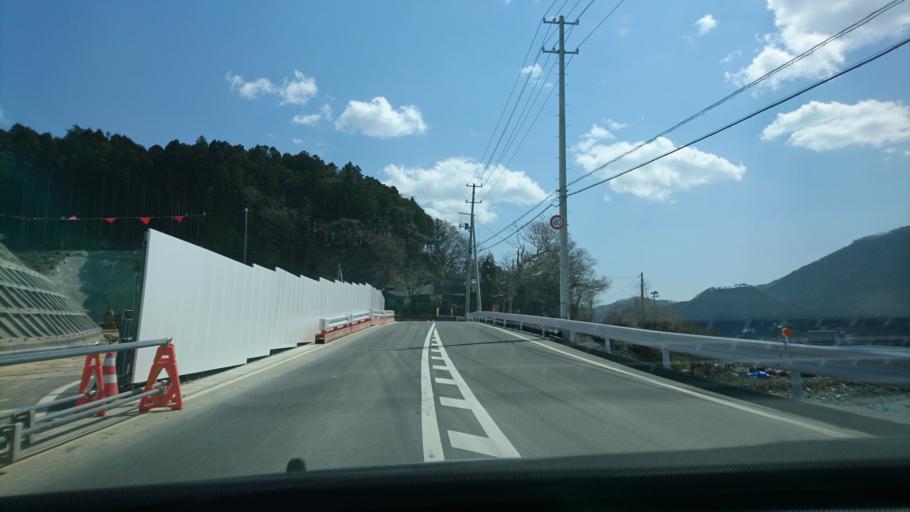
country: JP
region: Miyagi
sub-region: Oshika Gun
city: Onagawa Cho
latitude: 38.4449
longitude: 141.4628
